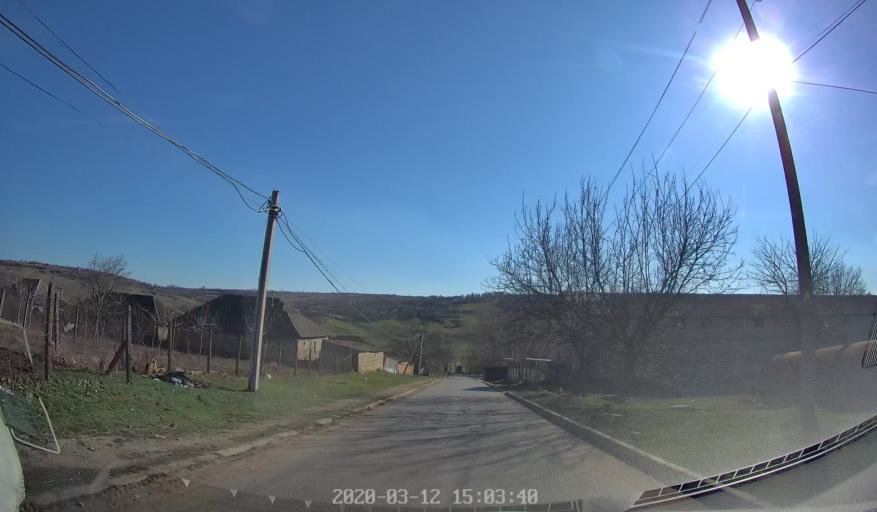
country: MD
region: Telenesti
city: Cocieri
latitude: 47.2227
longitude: 29.0196
